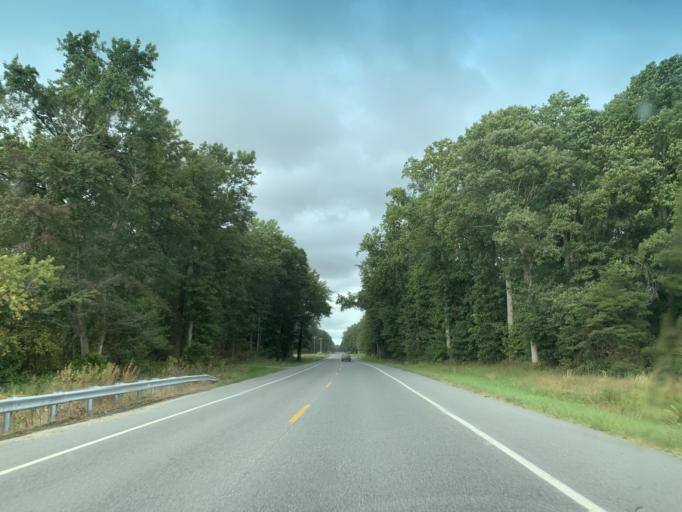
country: US
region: Maryland
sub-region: Caroline County
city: Ridgely
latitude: 39.0082
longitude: -75.8732
